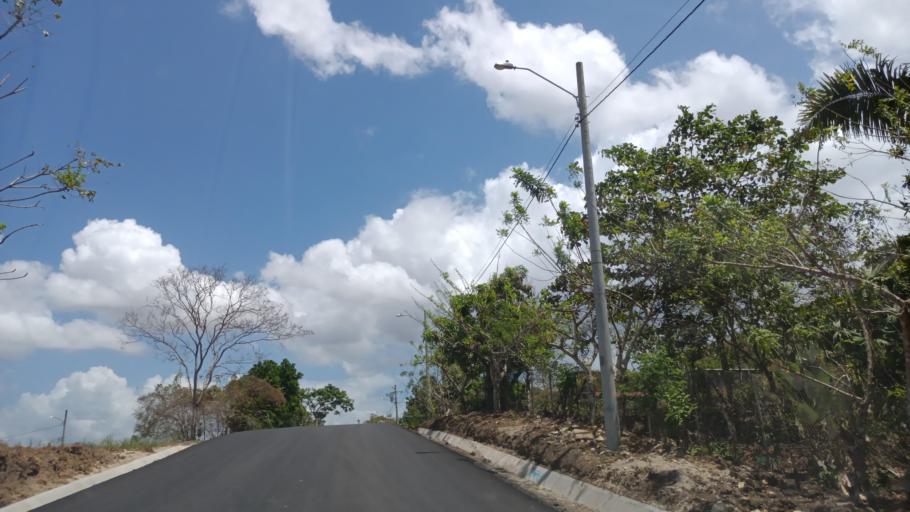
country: PA
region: Panama
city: Alcalde Diaz
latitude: 9.0967
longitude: -79.5750
